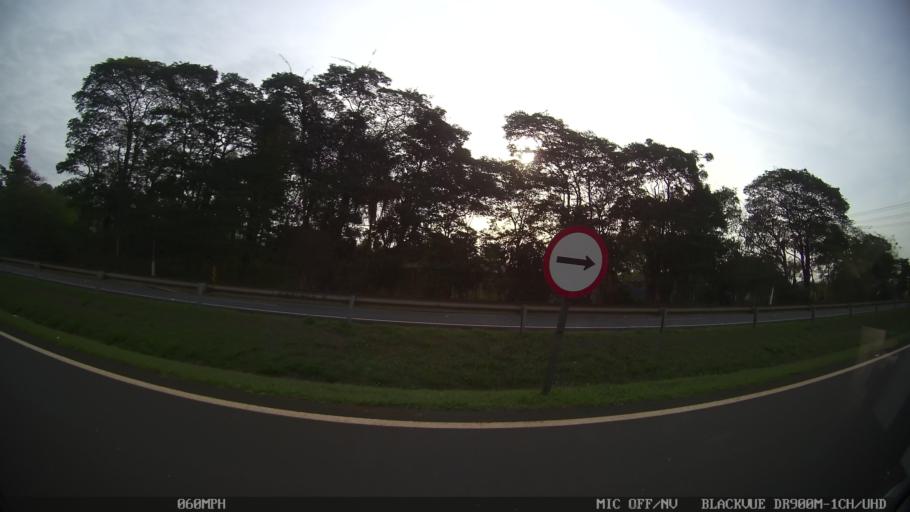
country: BR
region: Sao Paulo
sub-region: Iracemapolis
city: Iracemapolis
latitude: -22.6484
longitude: -47.5122
